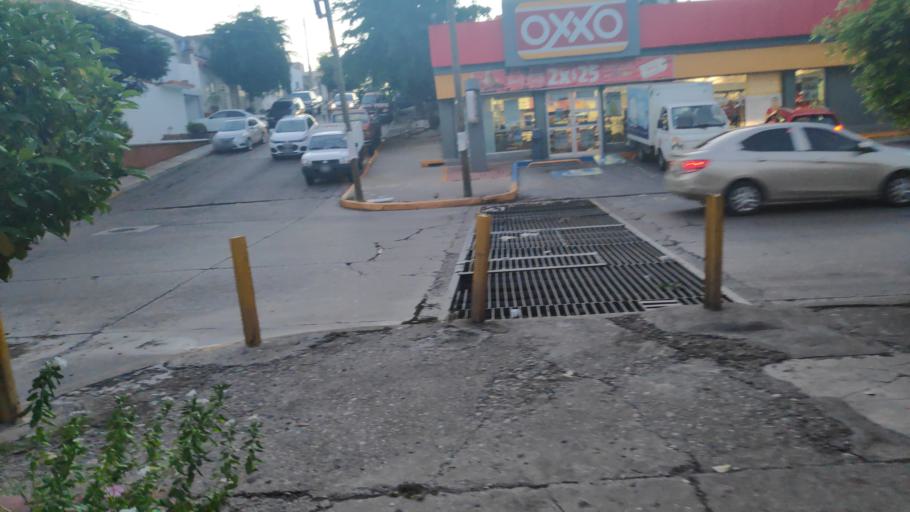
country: MX
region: Sinaloa
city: Culiacan
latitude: 24.7905
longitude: -107.4083
